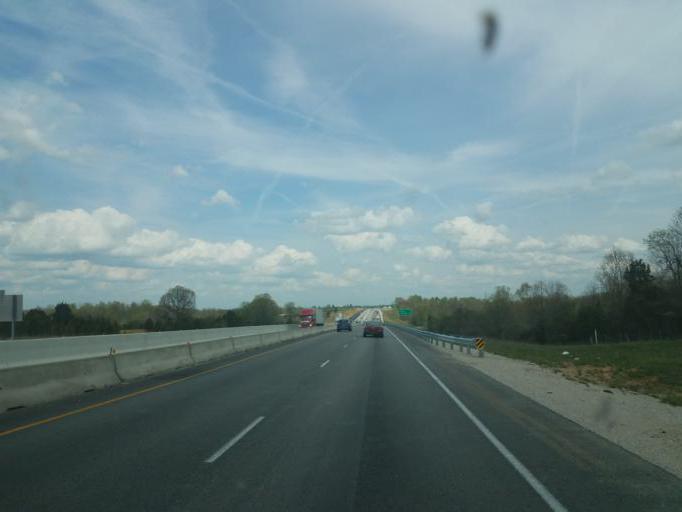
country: US
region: Kentucky
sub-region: Larue County
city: Hodgenville
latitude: 37.4723
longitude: -85.8817
